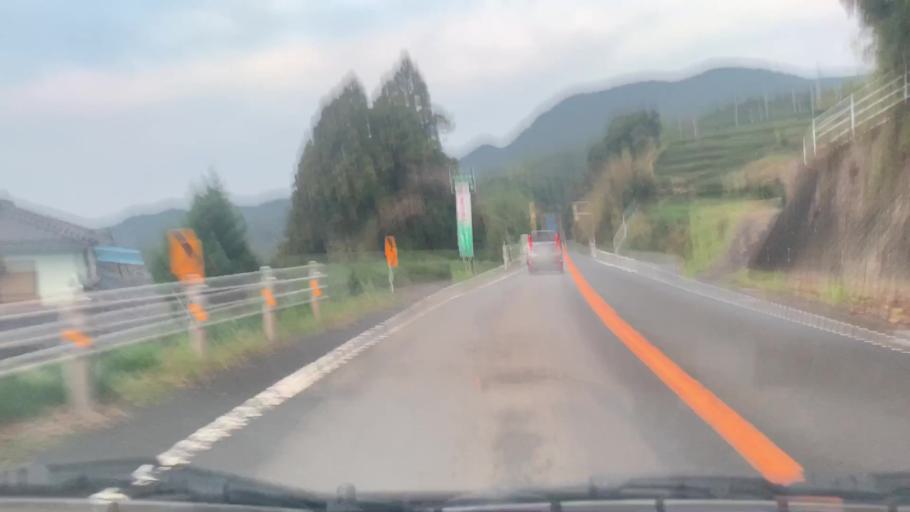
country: JP
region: Saga Prefecture
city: Ureshinomachi-shimojuku
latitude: 33.0608
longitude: 129.9581
